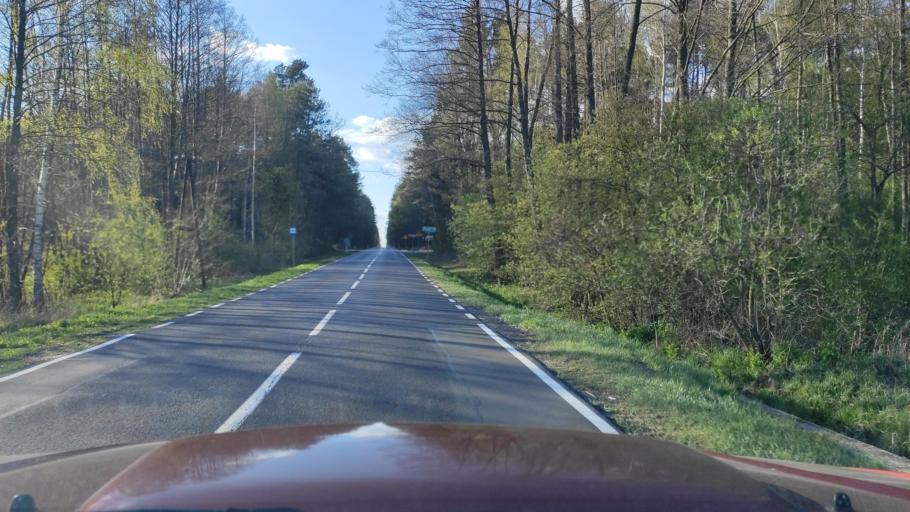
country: PL
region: Masovian Voivodeship
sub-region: Powiat zwolenski
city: Zwolen
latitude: 51.3865
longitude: 21.5539
